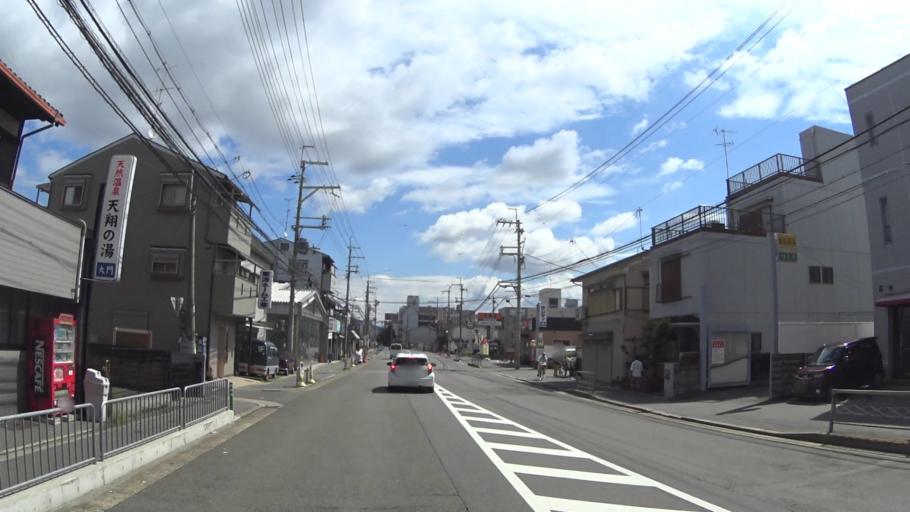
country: JP
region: Kyoto
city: Muko
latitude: 34.9888
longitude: 135.7261
